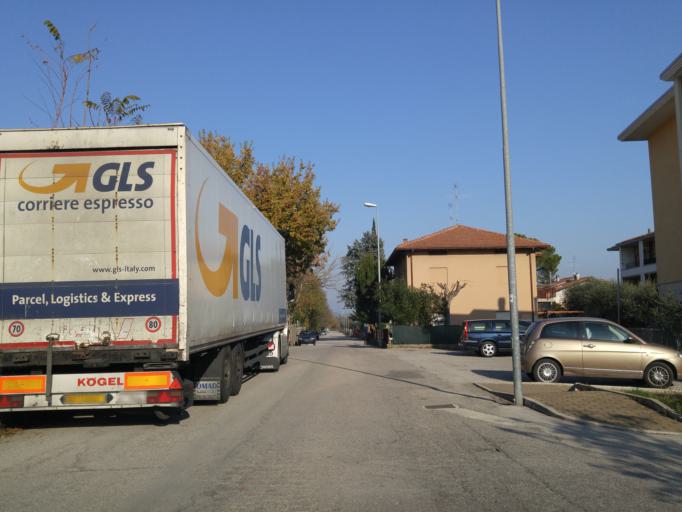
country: IT
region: The Marches
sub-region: Provincia di Pesaro e Urbino
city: Calcinelli
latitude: 43.7523
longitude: 12.9207
